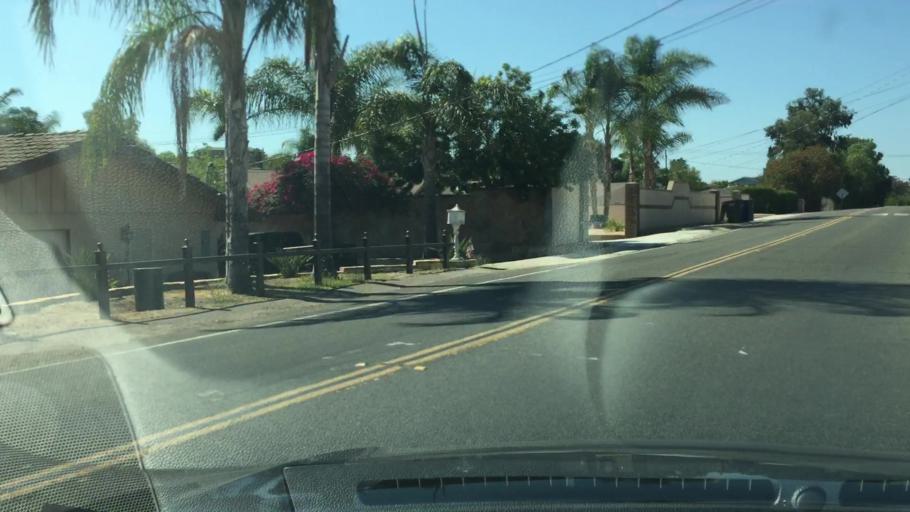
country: US
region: California
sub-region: San Diego County
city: Jamul
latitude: 32.7255
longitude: -116.8696
